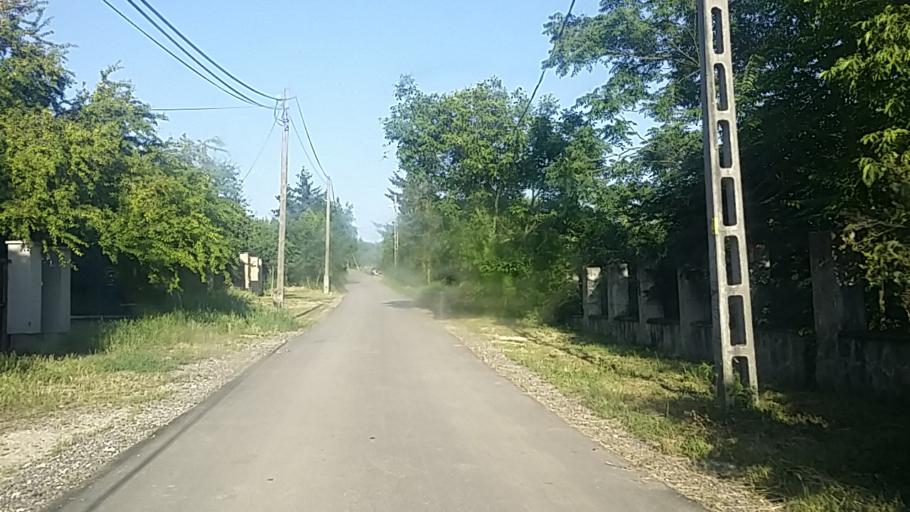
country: HU
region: Pest
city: Urom
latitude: 47.5784
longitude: 19.0179
